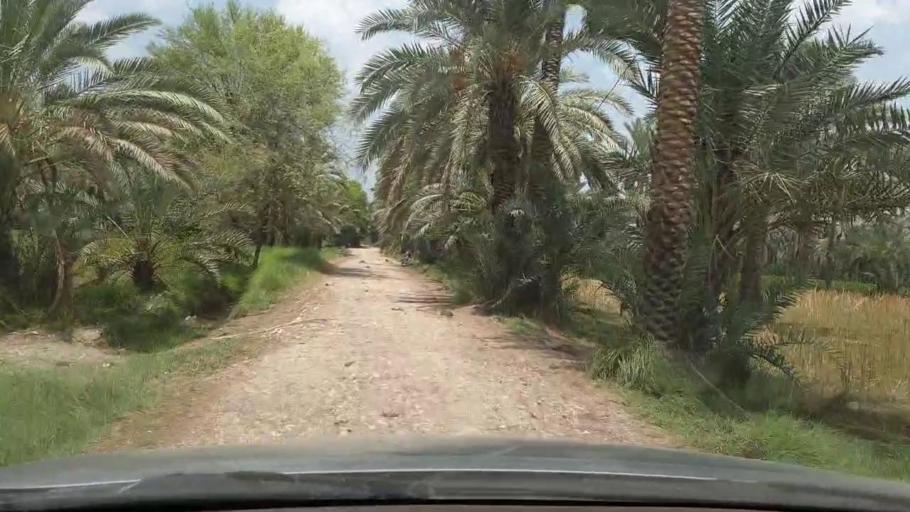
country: PK
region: Sindh
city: Kot Diji
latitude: 27.4255
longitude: 68.7683
